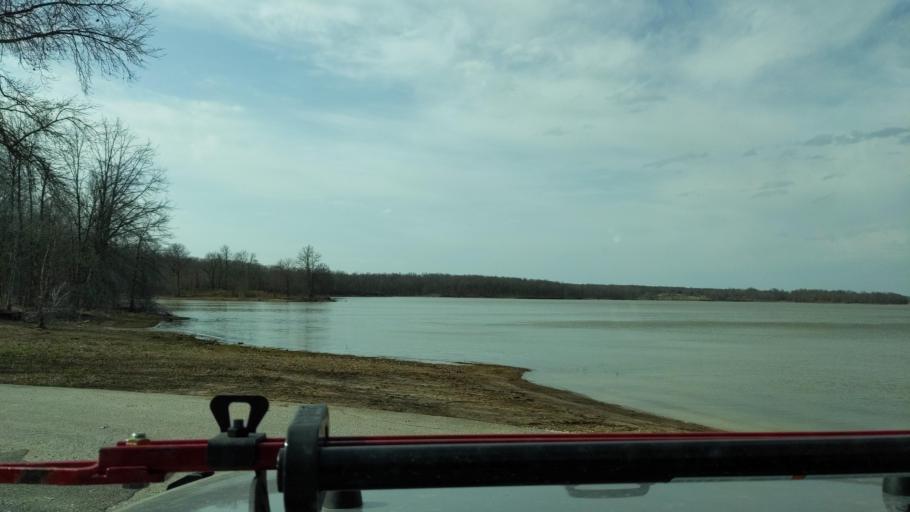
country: US
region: Missouri
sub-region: Macon County
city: Macon
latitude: 39.7721
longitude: -92.5206
